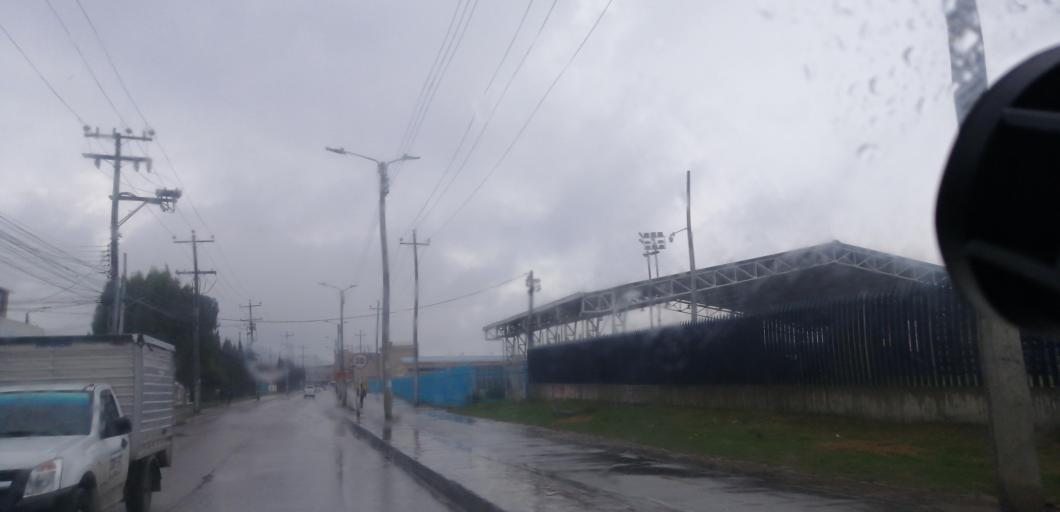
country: CO
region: Cundinamarca
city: Madrid
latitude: 4.7383
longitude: -74.2555
